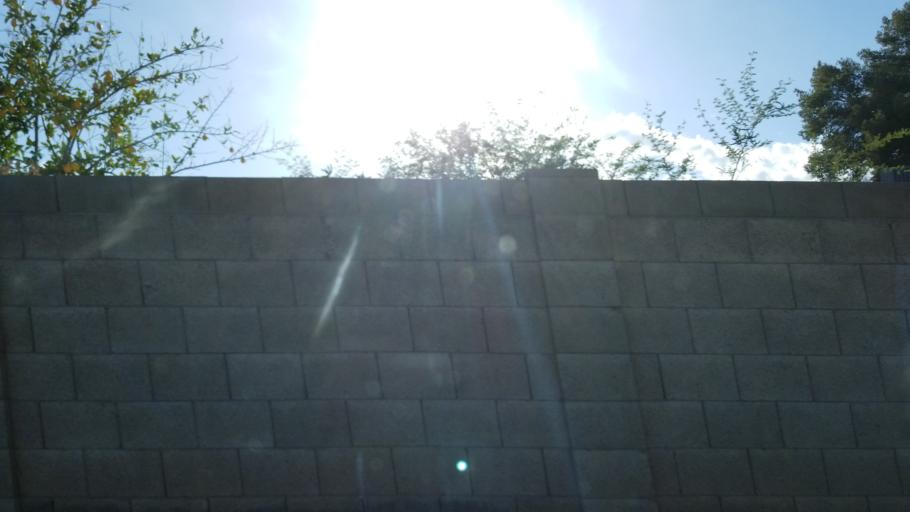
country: US
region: Arizona
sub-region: Maricopa County
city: Glendale
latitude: 33.6456
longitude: -112.0657
